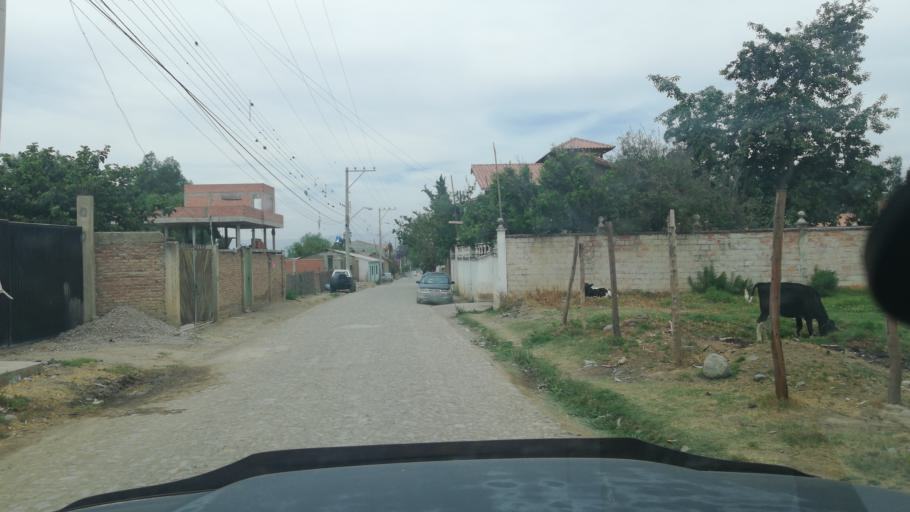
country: BO
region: Cochabamba
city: Cochabamba
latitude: -17.3519
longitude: -66.2193
